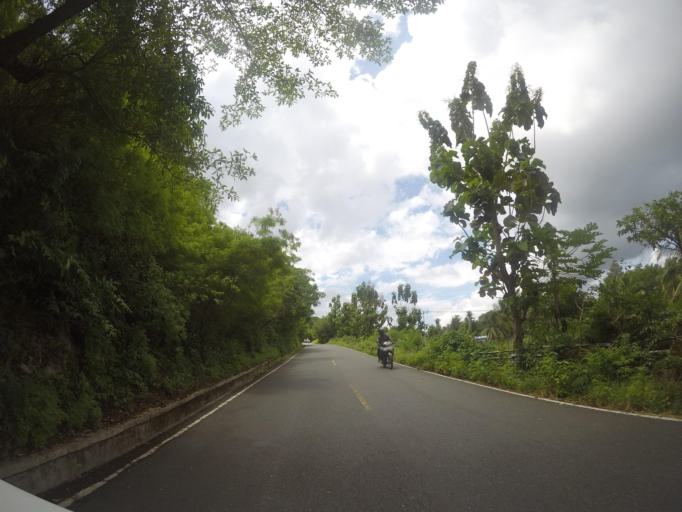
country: TL
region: Bobonaro
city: Maliana
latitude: -8.9557
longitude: 125.0659
